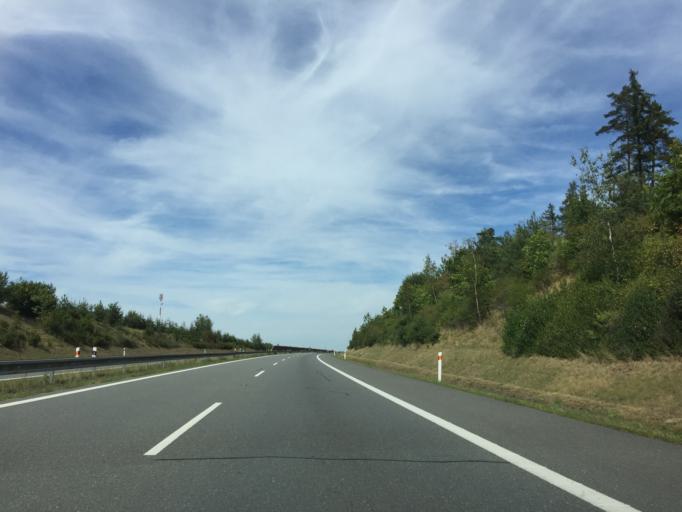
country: CZ
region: Jihocesky
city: Chotoviny
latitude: 49.4990
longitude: 14.6601
